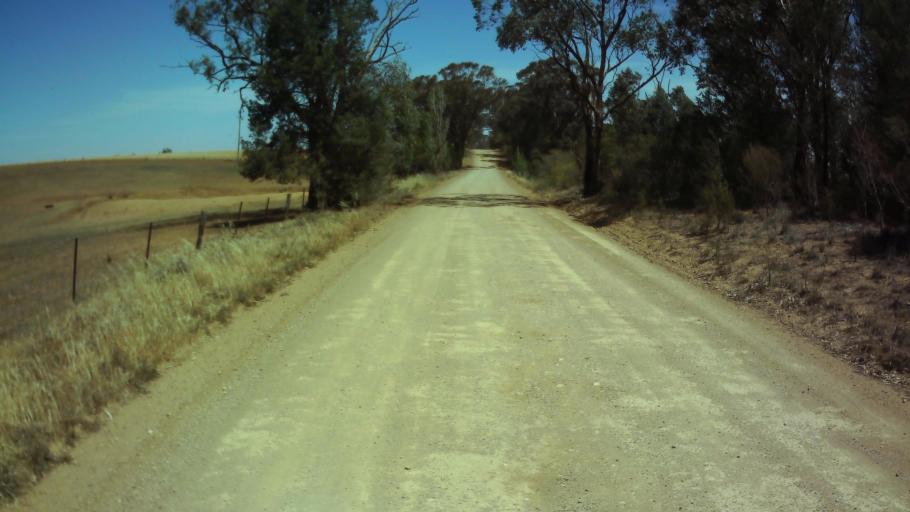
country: AU
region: New South Wales
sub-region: Weddin
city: Grenfell
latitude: -33.9132
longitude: 148.1783
